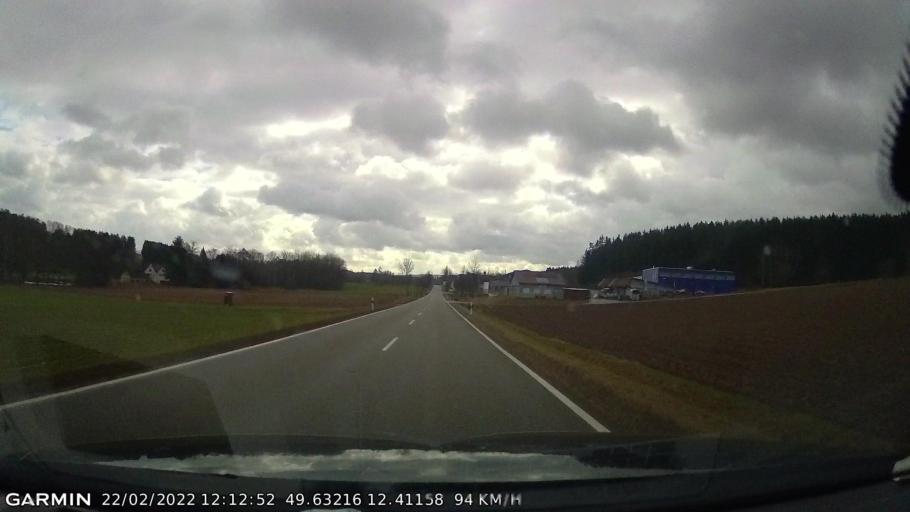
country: DE
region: Bavaria
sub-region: Upper Palatinate
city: Pleystein
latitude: 49.6318
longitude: 12.4117
